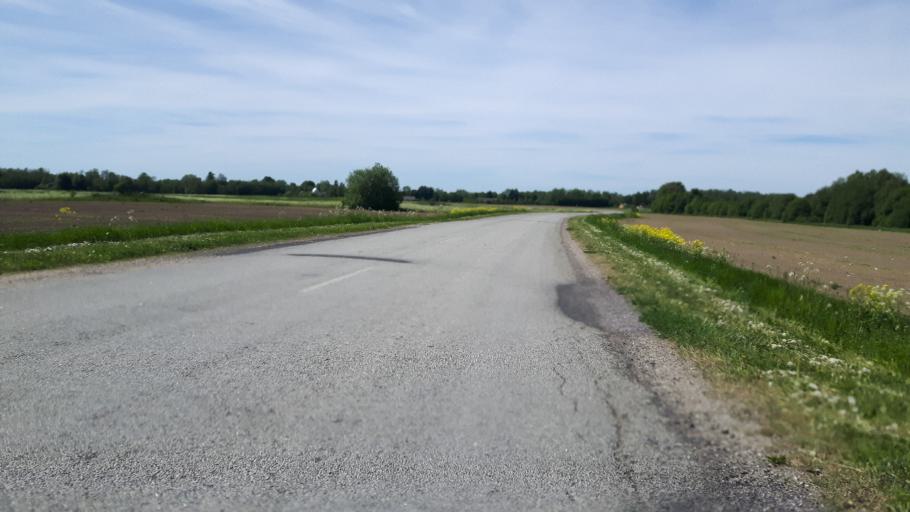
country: EE
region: Harju
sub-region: Kuusalu vald
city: Kuusalu
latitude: 59.4540
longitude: 25.3663
